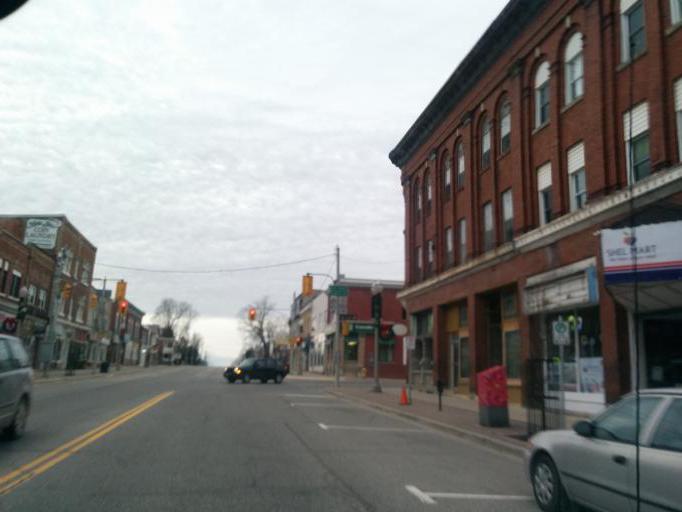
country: CA
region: Ontario
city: Shelburne
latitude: 44.0784
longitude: -80.2041
